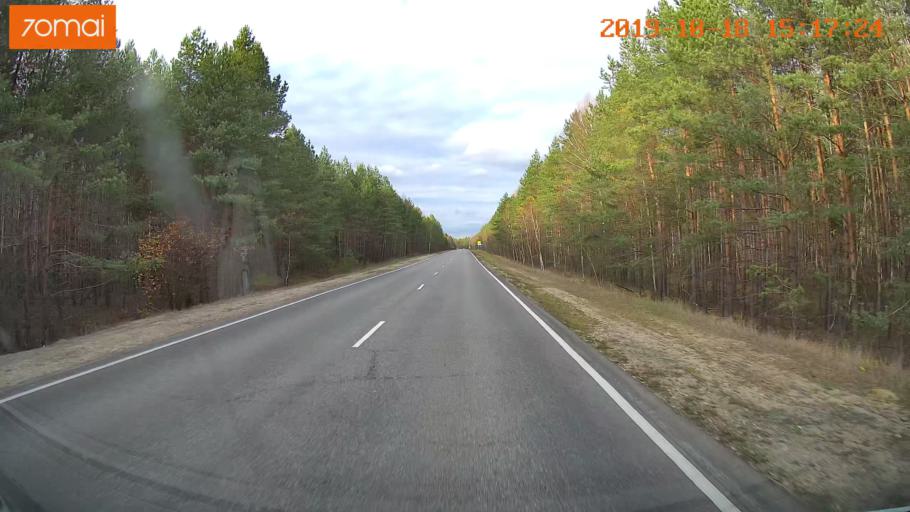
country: RU
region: Vladimir
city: Anopino
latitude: 55.6491
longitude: 40.7265
